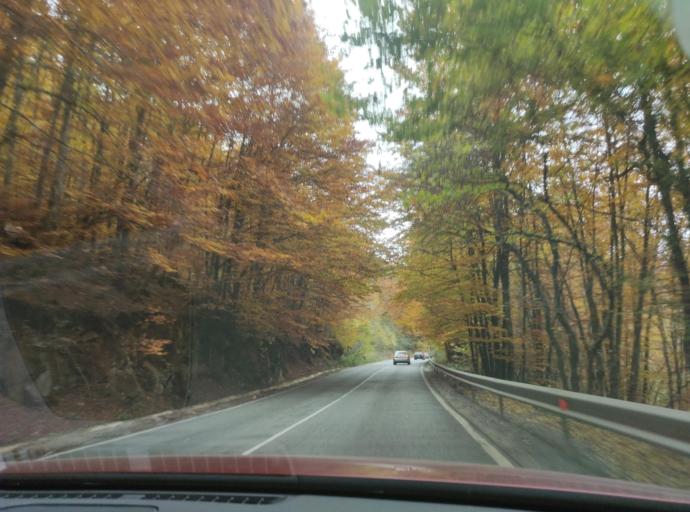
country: BG
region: Sofiya
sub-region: Obshtina Godech
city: Godech
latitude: 43.0258
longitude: 23.1368
